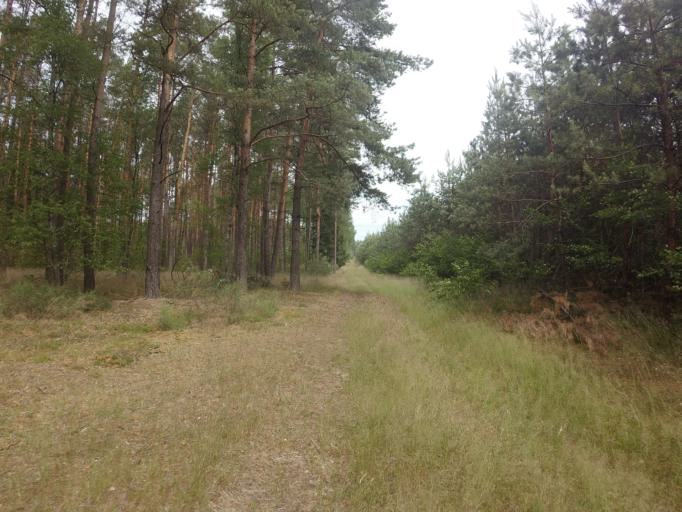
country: PL
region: West Pomeranian Voivodeship
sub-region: Powiat choszczenski
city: Bierzwnik
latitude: 53.1126
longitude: 15.6735
